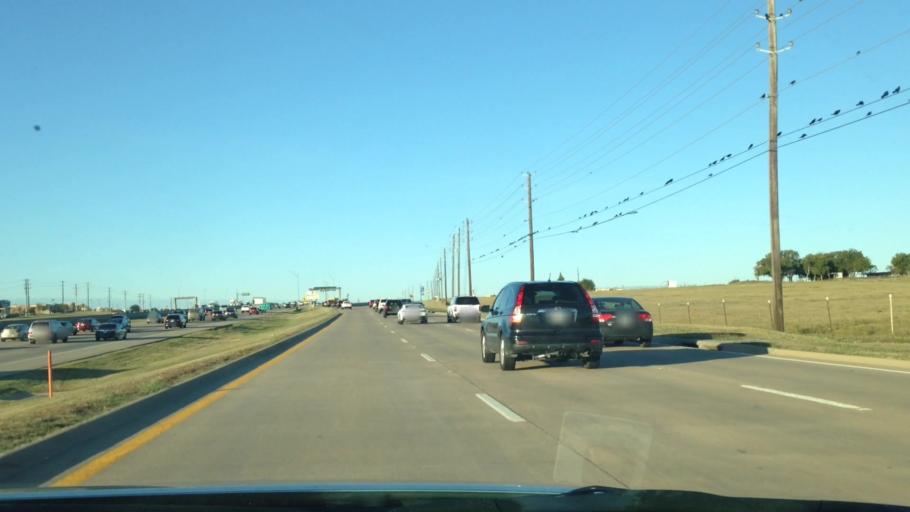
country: US
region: Texas
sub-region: Collin County
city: Frisco
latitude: 33.1160
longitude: -96.7599
